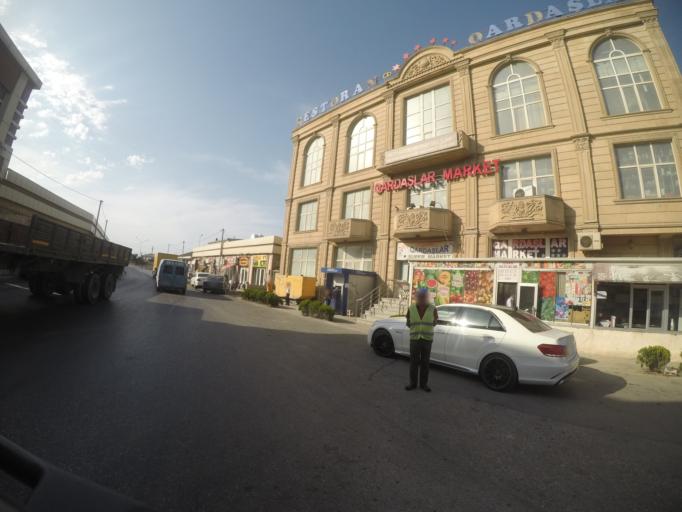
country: AZ
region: Baki
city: Binagadi
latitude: 40.4677
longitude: 49.8421
